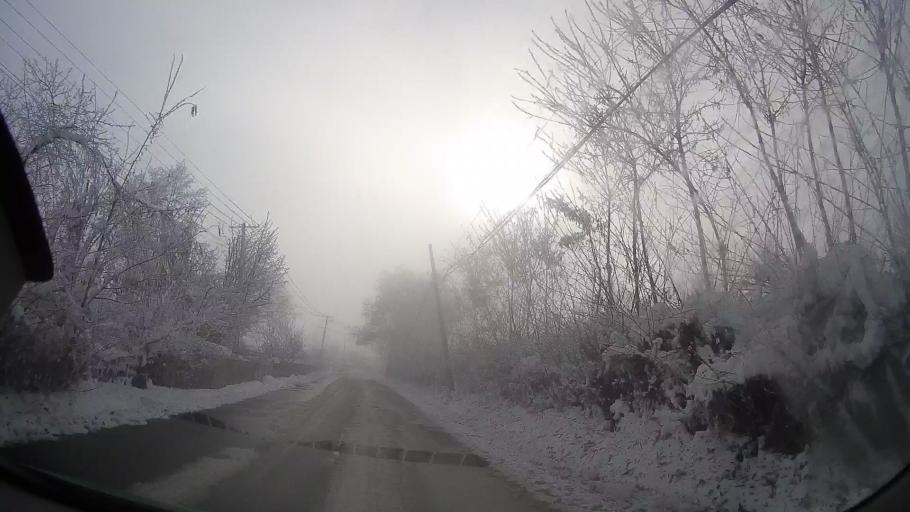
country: RO
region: Iasi
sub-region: Comuna Valea Seaca
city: Topile
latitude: 47.2550
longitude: 26.6664
